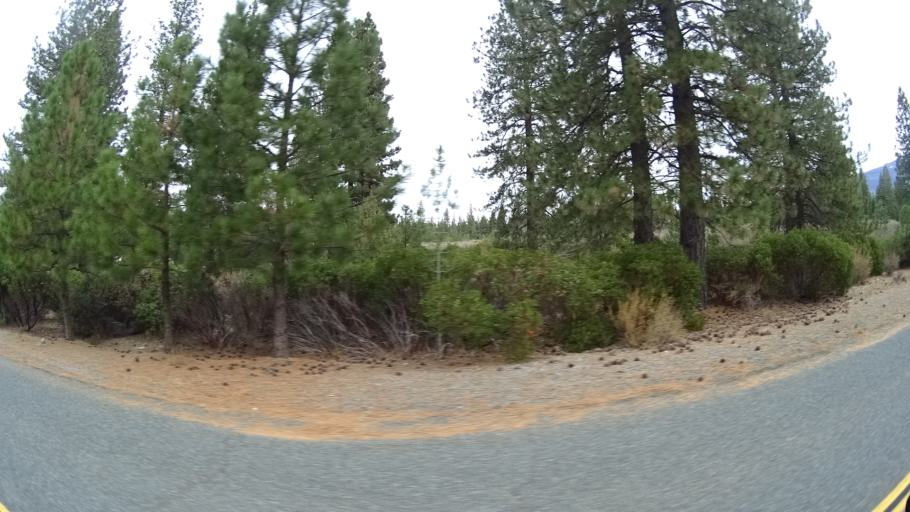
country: US
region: California
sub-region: Siskiyou County
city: Weed
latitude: 41.4081
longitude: -122.3703
